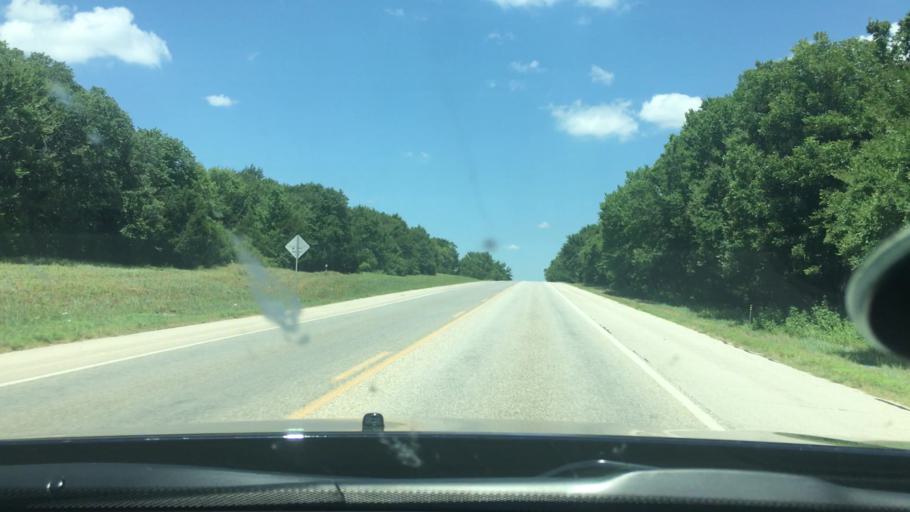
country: US
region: Oklahoma
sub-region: Marshall County
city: Oakland
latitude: 34.1770
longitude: -96.8603
